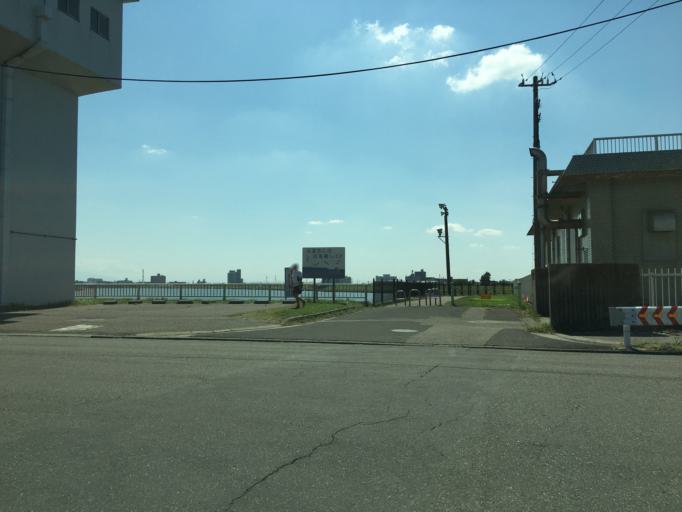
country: JP
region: Niigata
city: Niigata-shi
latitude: 37.8973
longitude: 139.0122
